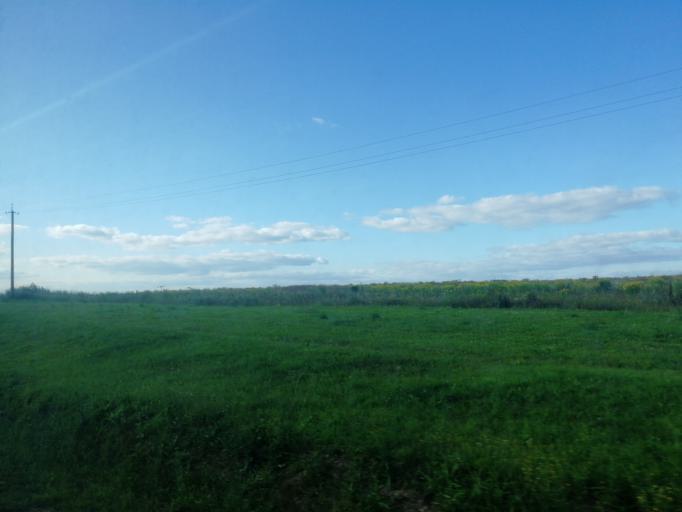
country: RU
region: Tula
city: Leninskiy
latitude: 54.2395
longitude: 37.3422
